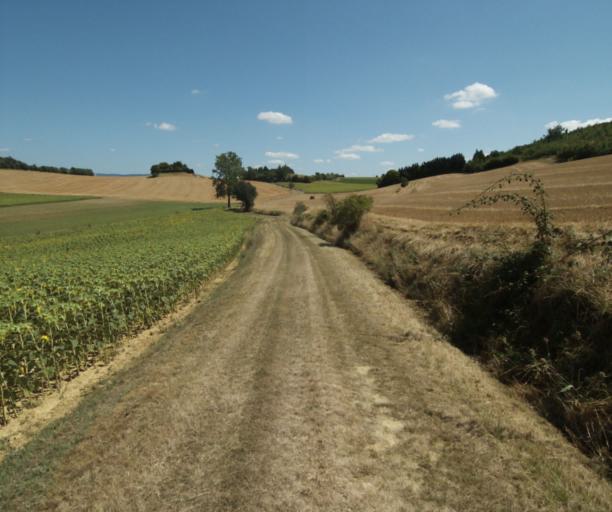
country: FR
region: Midi-Pyrenees
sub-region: Departement de la Haute-Garonne
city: Saint-Felix-Lauragais
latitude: 43.4576
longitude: 1.8860
